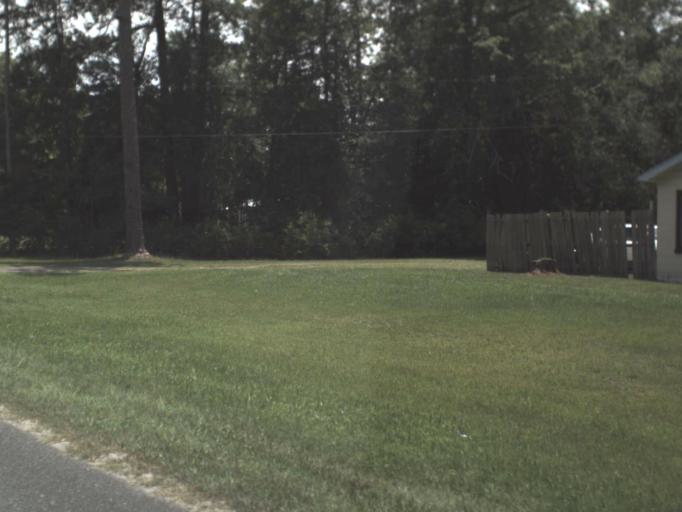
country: US
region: Florida
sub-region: Bradford County
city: Starke
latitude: 29.9689
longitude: -82.1207
